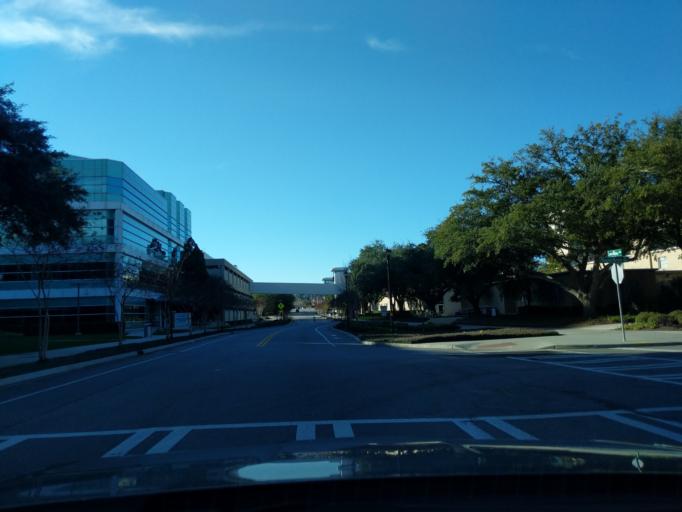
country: US
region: Georgia
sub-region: Richmond County
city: Augusta
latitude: 33.4691
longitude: -81.9888
